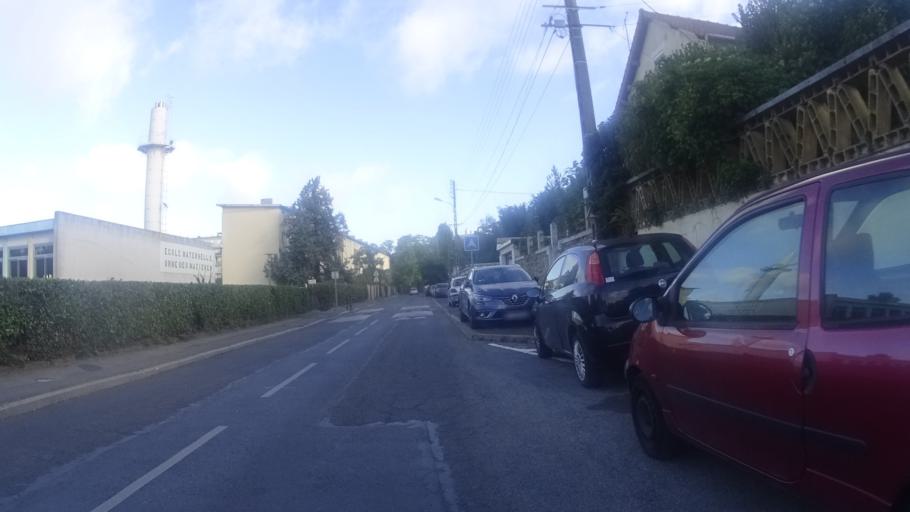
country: FR
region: Ile-de-France
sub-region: Departement de l'Essonne
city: Draveil
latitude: 48.6793
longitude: 2.4032
